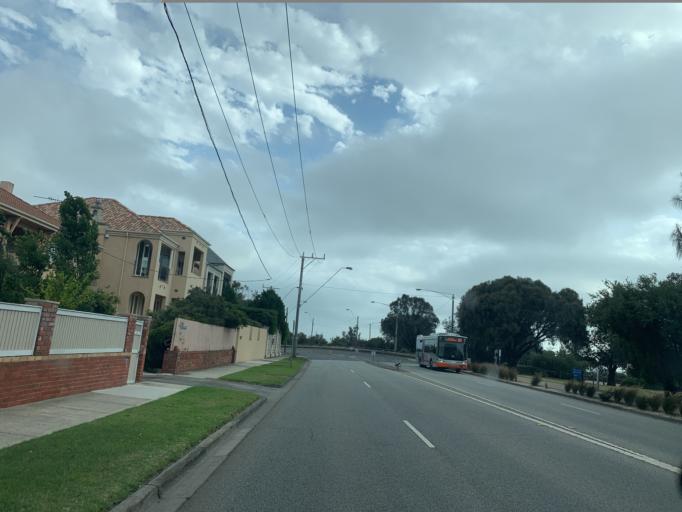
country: AU
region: Victoria
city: Hampton
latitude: -37.9476
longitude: 145.0007
